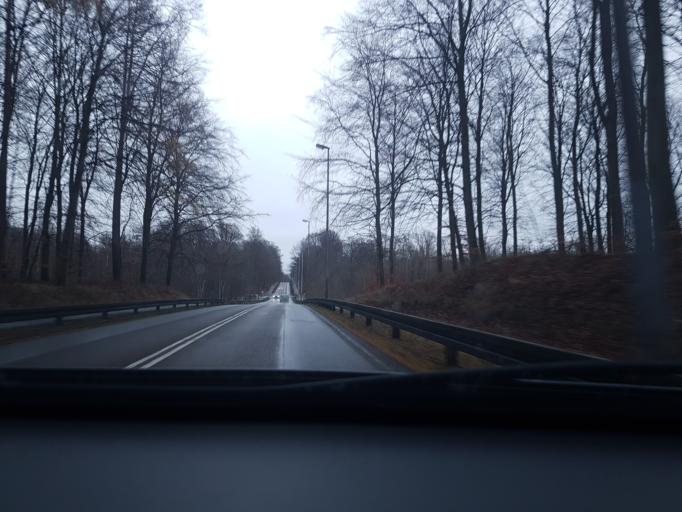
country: DK
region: Capital Region
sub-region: Fureso Kommune
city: Vaerlose
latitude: 55.7606
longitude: 12.3687
